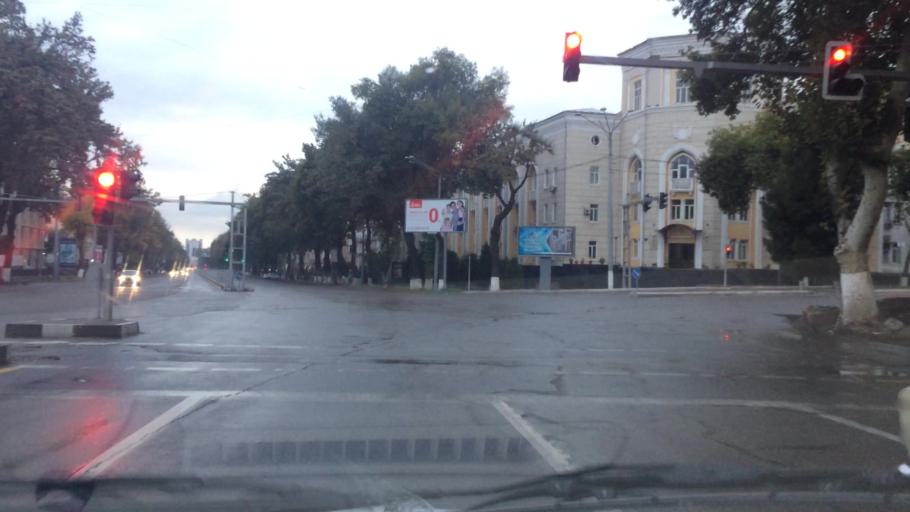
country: UZ
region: Toshkent Shahri
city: Tashkent
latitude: 41.3204
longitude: 69.2652
